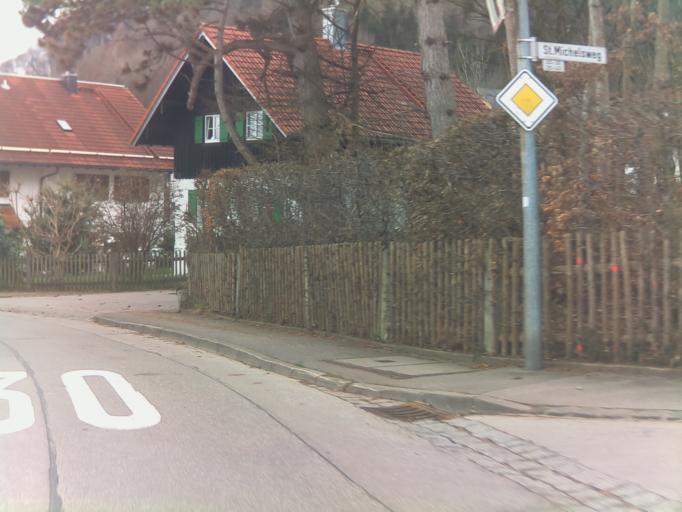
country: DE
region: Bavaria
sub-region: Upper Bavaria
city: Peissenberg
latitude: 47.8010
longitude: 11.0581
